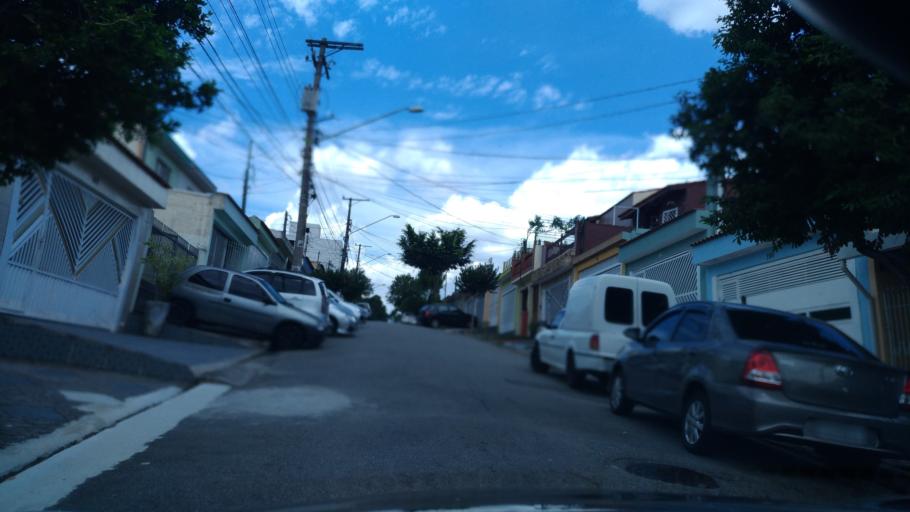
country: BR
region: Sao Paulo
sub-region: Sao Bernardo Do Campo
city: Sao Bernardo do Campo
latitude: -23.7051
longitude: -46.5808
